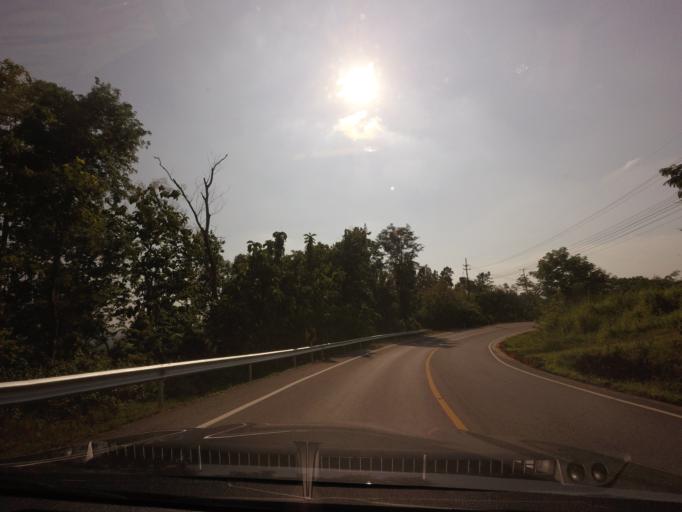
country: TH
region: Nan
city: Santi Suk
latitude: 18.9068
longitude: 100.8584
